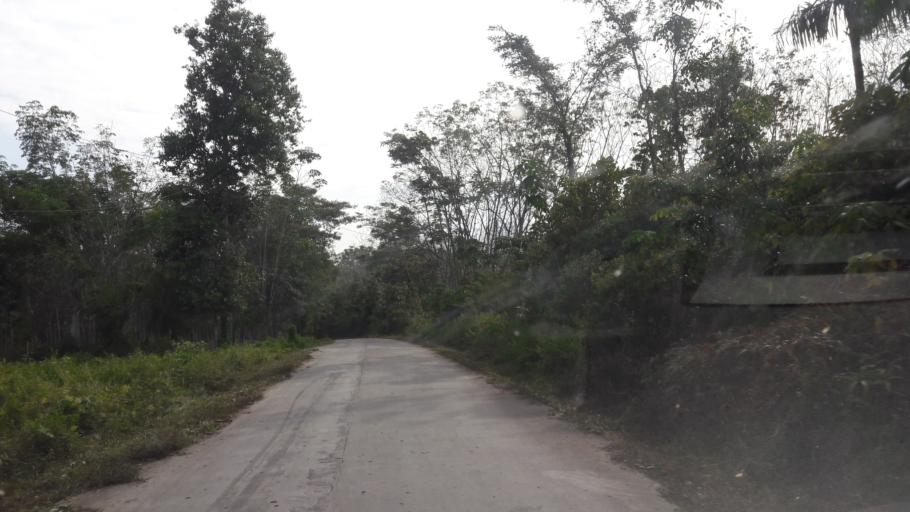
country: ID
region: South Sumatra
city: Gunungmenang
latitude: -3.1046
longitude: 103.9885
